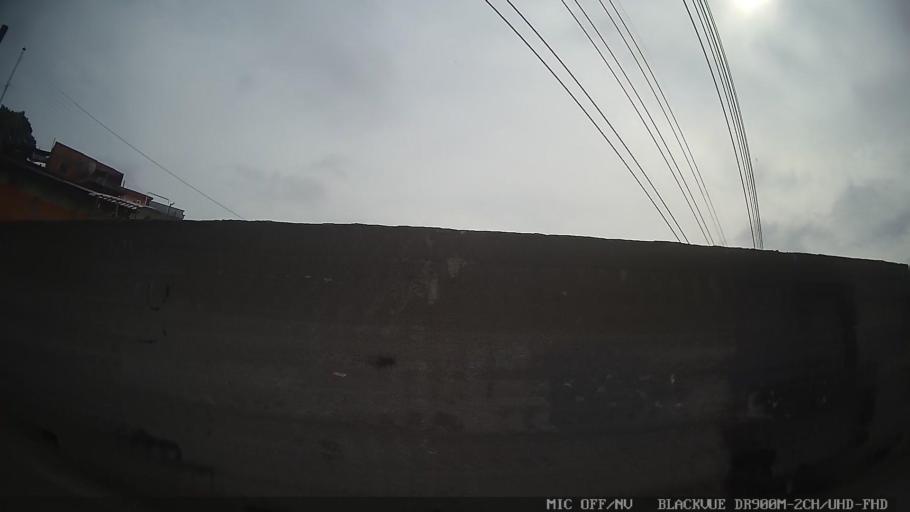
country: BR
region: Sao Paulo
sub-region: Poa
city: Poa
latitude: -23.5229
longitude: -46.3495
